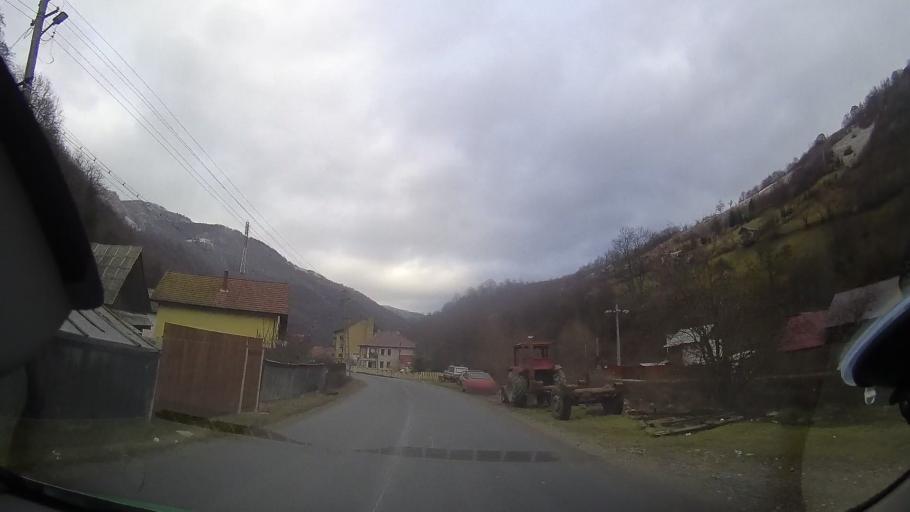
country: RO
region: Cluj
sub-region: Comuna Maguri-Racatau
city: Maguri-Racatau
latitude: 46.6459
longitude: 23.1951
